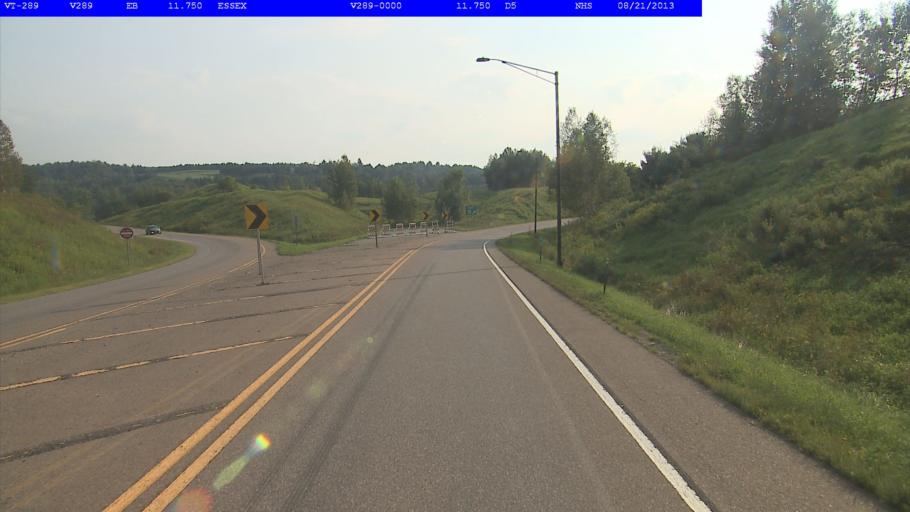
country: US
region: Vermont
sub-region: Chittenden County
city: Essex Junction
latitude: 44.4839
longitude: -73.0672
